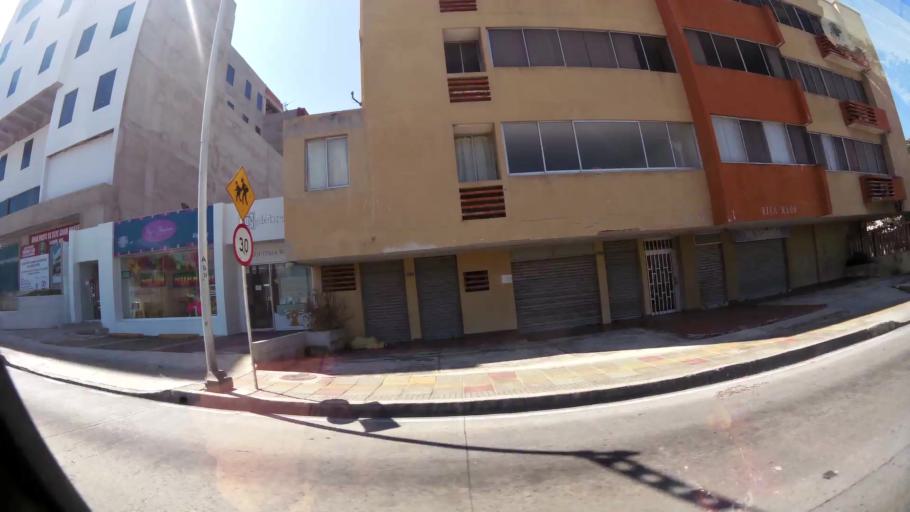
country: CO
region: Atlantico
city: Barranquilla
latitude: 11.0083
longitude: -74.8230
